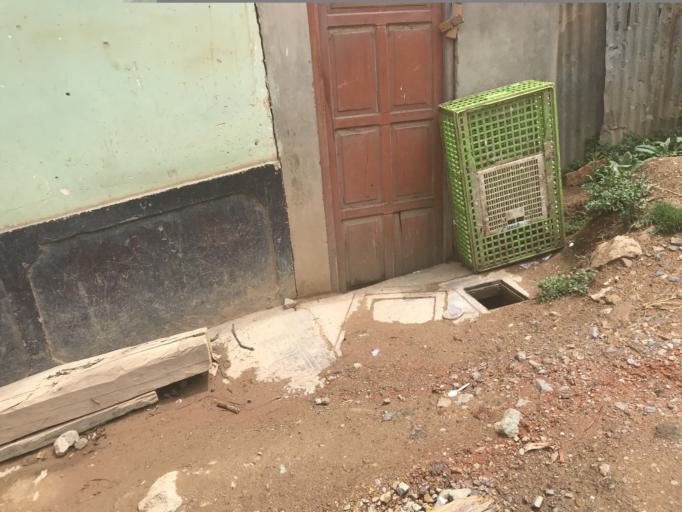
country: PE
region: Cajamarca
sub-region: Provincia de Chota
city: Querocoto
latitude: -6.3584
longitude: -79.0350
